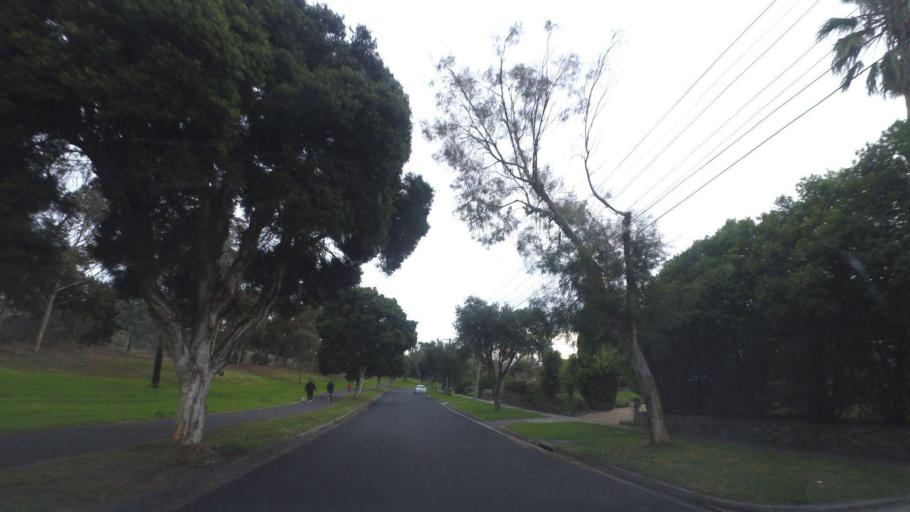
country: AU
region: Victoria
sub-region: Boroondara
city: Balwyn North
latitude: -37.7793
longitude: 145.0913
